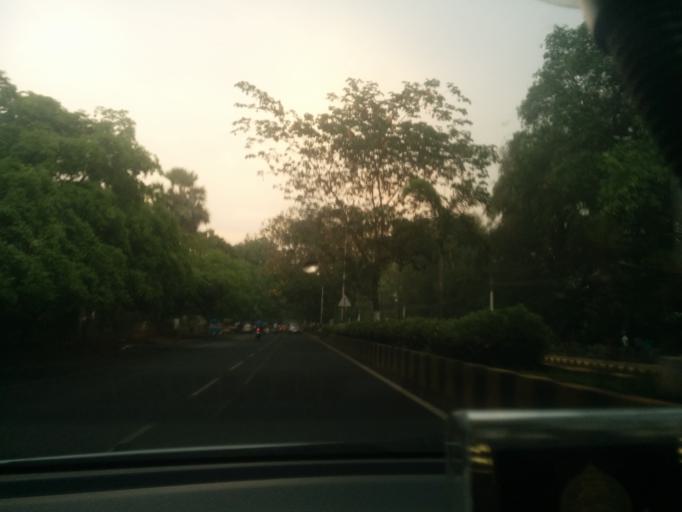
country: IN
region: Andhra Pradesh
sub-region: East Godavari
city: Rajahmundry
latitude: 17.0163
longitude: 81.7881
